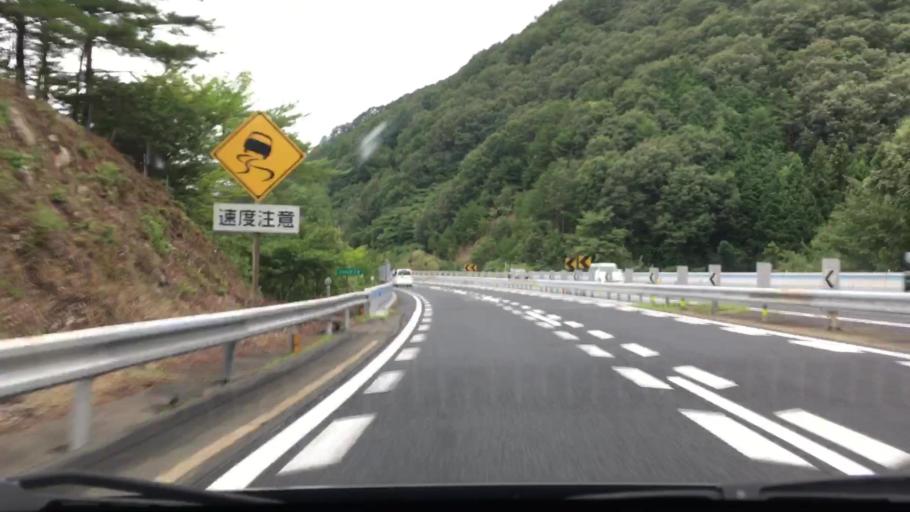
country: JP
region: Hiroshima
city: Miyoshi
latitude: 34.6918
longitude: 132.5842
